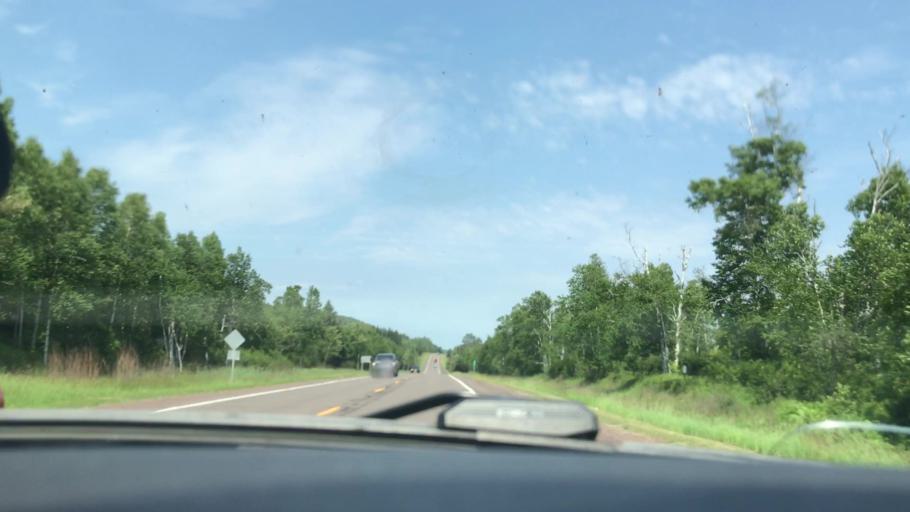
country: US
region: Minnesota
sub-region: Lake County
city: Silver Bay
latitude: 47.4408
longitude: -91.0733
